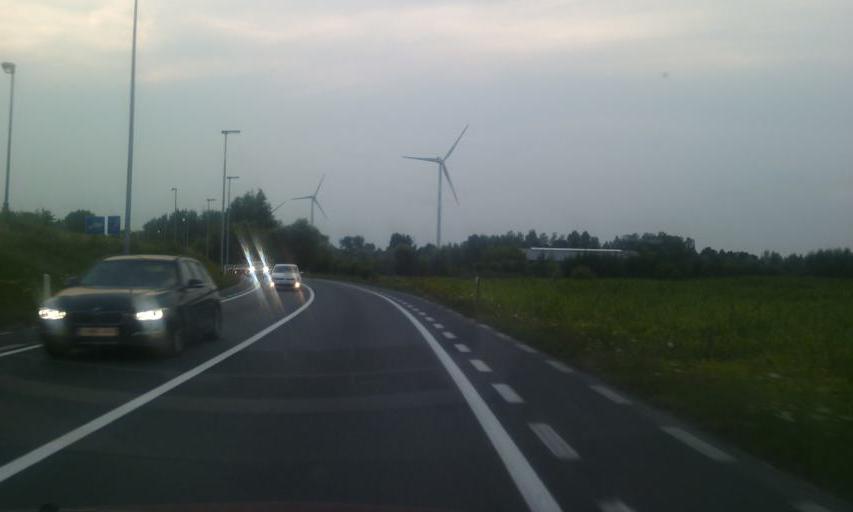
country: BE
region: Flanders
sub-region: Provincie Oost-Vlaanderen
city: Dendermonde
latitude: 51.0490
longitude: 4.0888
